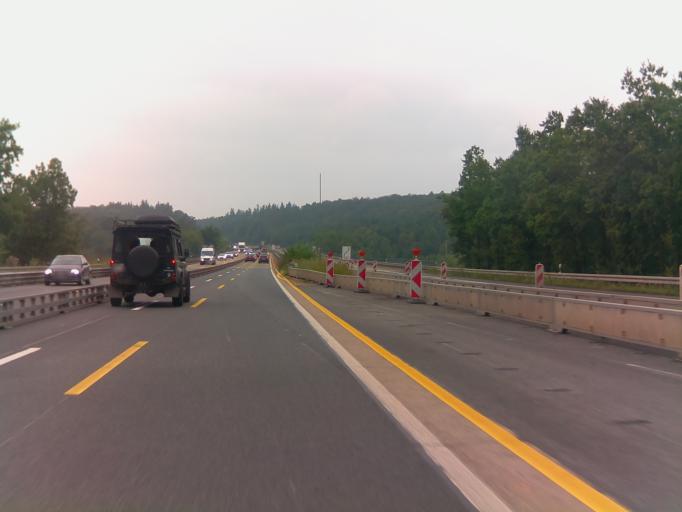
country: DE
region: Hesse
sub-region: Regierungsbezirk Kassel
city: Burghaun
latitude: 50.7265
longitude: 9.6476
